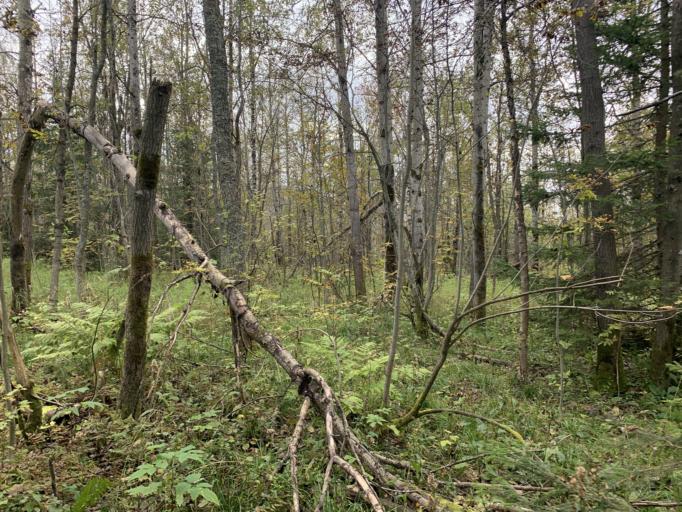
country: RU
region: Perm
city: Gubakha
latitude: 58.8469
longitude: 57.5797
